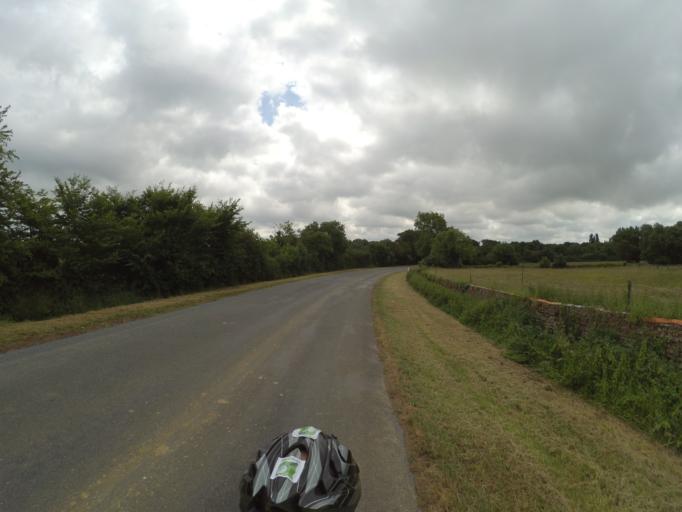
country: FR
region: Poitou-Charentes
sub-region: Departement de la Charente-Maritime
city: Saint-Laurent-de-la-Pree
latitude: 45.9949
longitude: -1.0358
